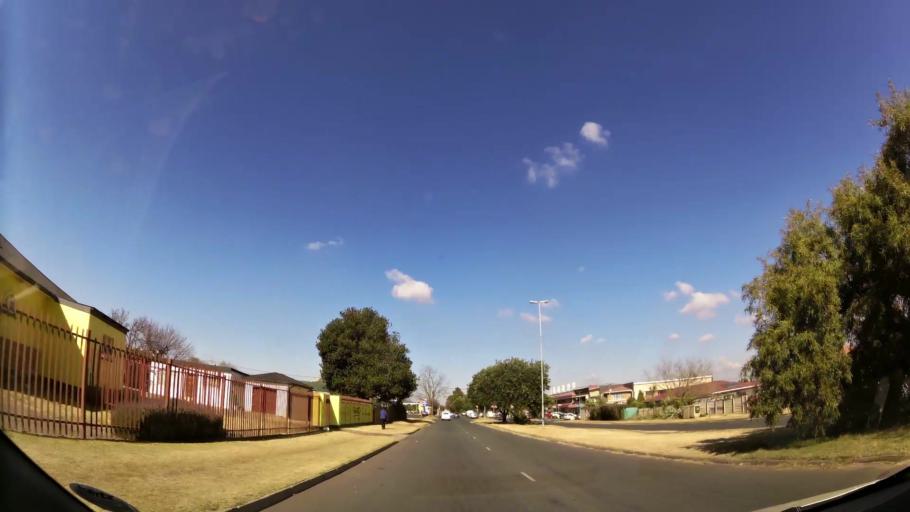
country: ZA
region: Gauteng
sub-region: City of Johannesburg Metropolitan Municipality
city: Roodepoort
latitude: -26.1323
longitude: 27.8355
